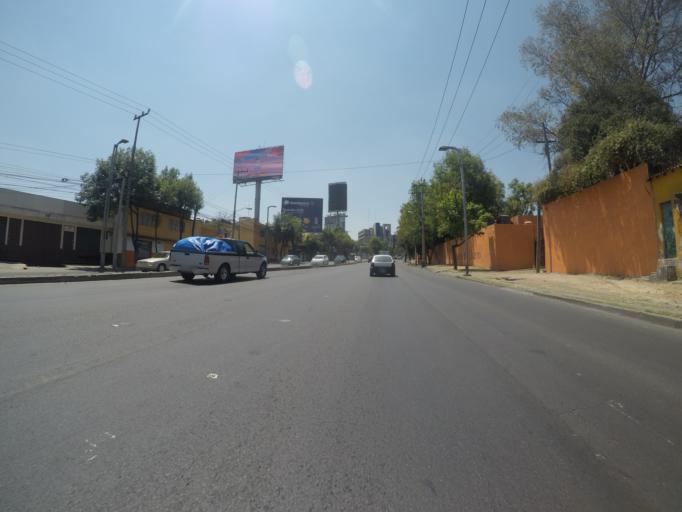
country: MX
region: Mexico City
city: Polanco
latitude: 19.3998
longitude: -99.2128
